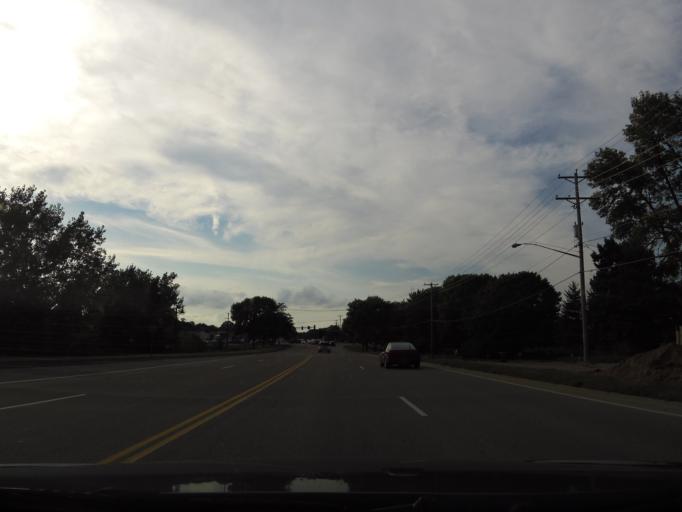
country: US
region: Minnesota
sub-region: Scott County
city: Prior Lake
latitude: 44.7127
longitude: -93.4204
